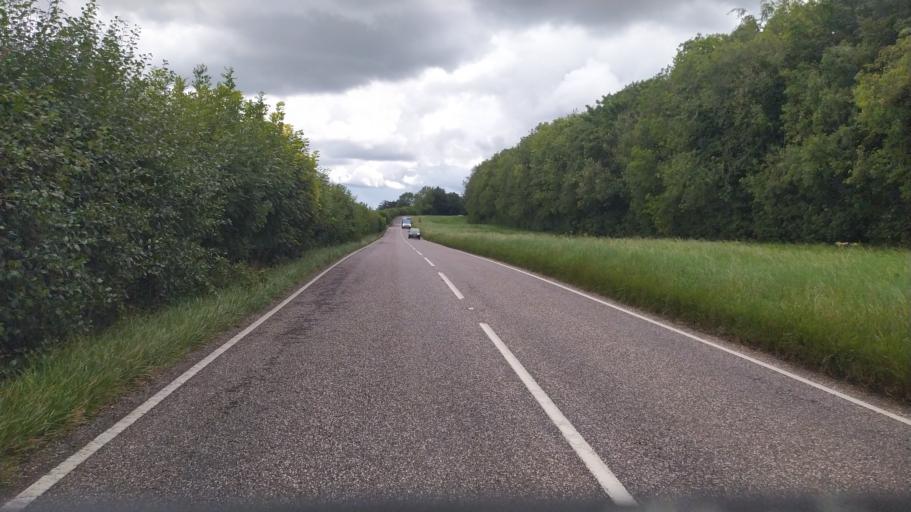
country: GB
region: England
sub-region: Wiltshire
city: Bower Chalke
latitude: 50.9256
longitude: -1.9493
